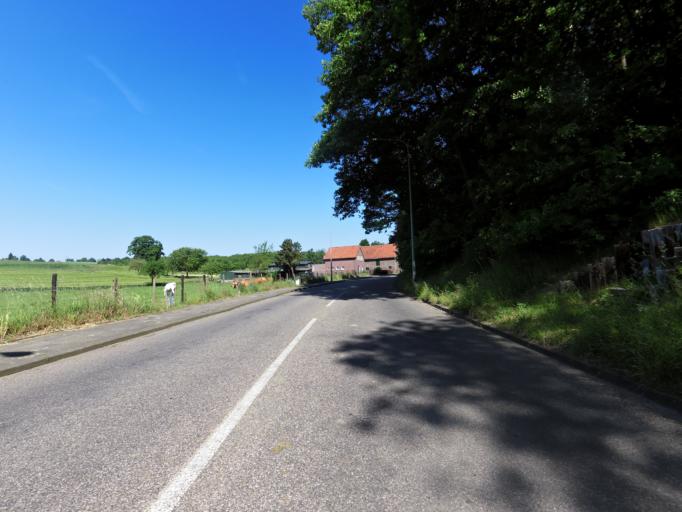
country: NL
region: Limburg
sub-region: Gemeente Kerkrade
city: Kerkrade
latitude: 50.9077
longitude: 6.0685
